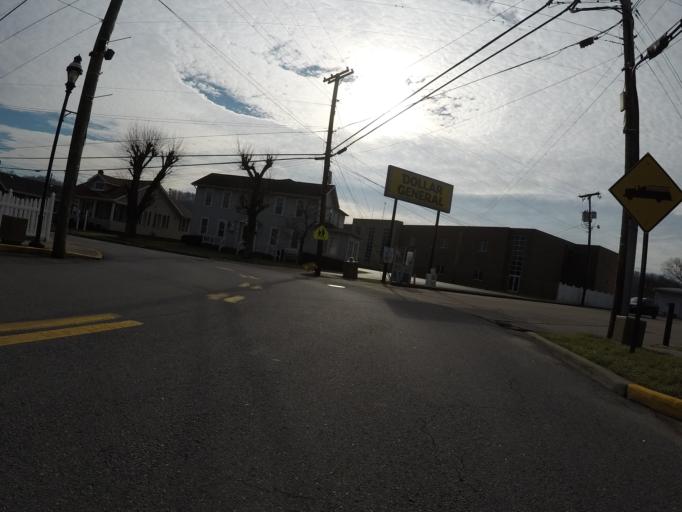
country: US
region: West Virginia
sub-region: Cabell County
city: Barboursville
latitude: 38.4083
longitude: -82.2959
